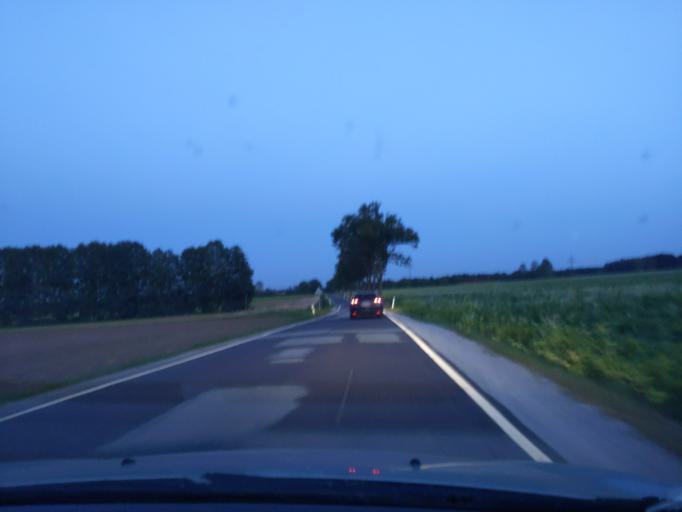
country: DE
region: Saxony
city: Grossdubrau
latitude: 51.3035
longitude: 14.4304
